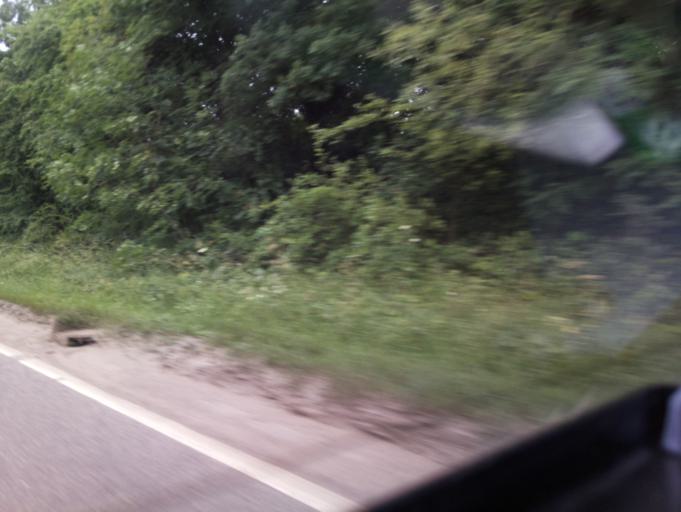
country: GB
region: England
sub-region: Warwickshire
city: Bedworth
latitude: 52.4925
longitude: -1.4811
